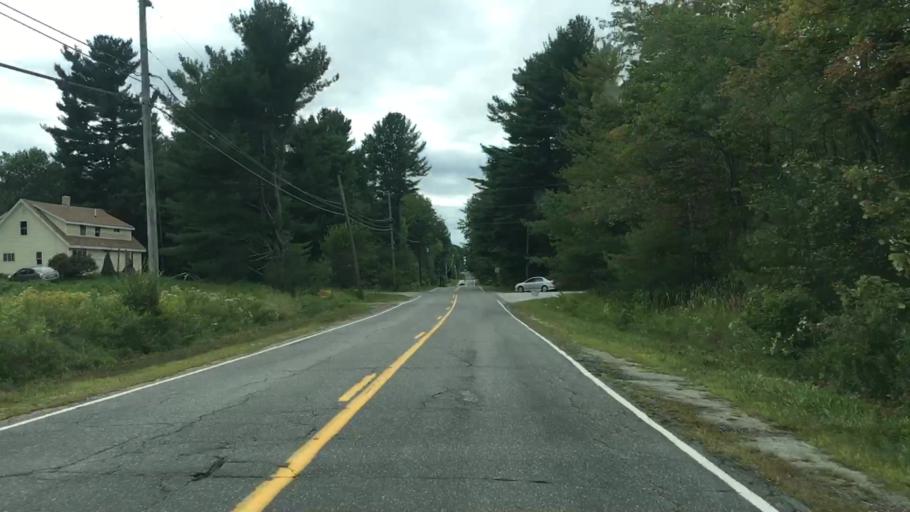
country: US
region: Maine
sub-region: Kennebec County
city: Hallowell
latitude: 44.2757
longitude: -69.8100
